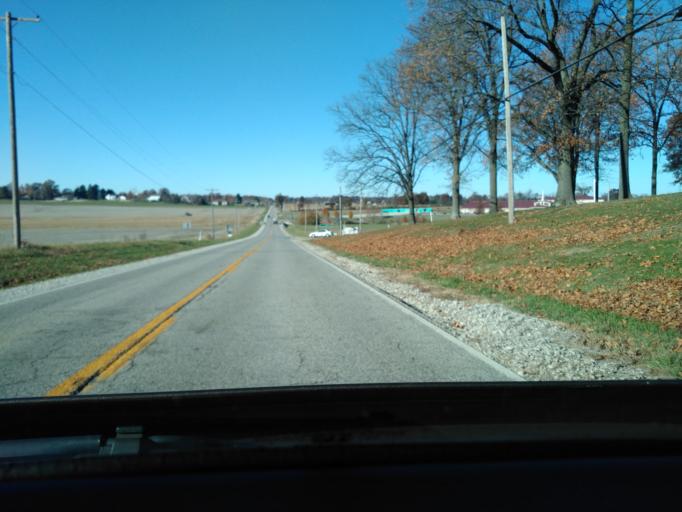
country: US
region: Illinois
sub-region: Bond County
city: Greenville
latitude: 38.9022
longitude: -89.3760
